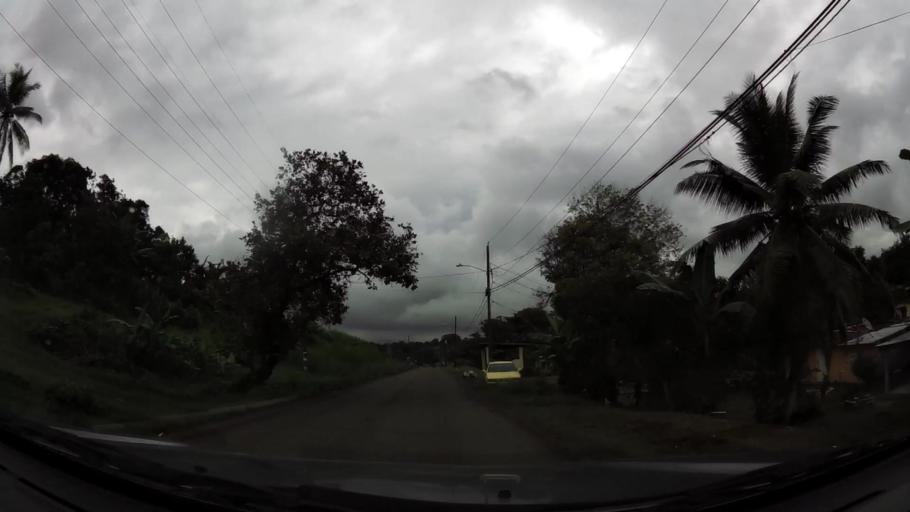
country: PA
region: Panama
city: Chilibre
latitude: 9.1859
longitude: -79.6124
